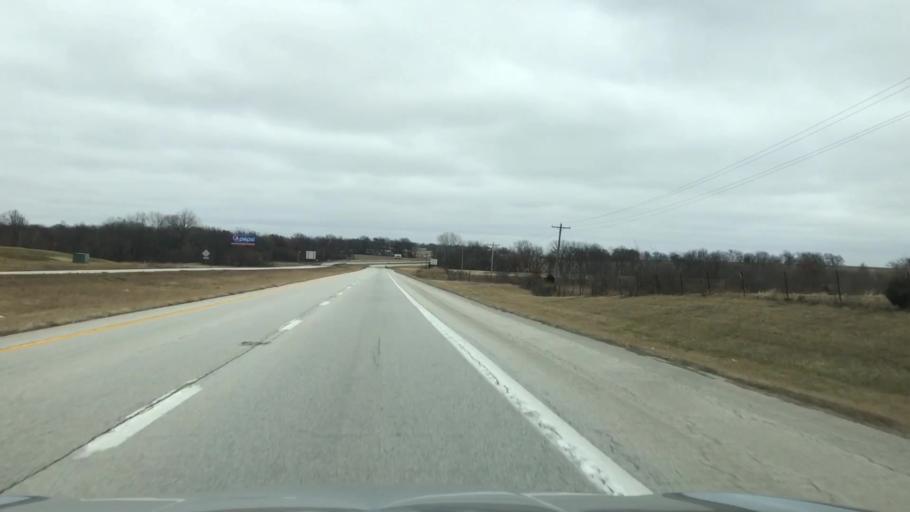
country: US
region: Missouri
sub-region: Livingston County
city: Chillicothe
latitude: 39.7736
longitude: -93.5359
